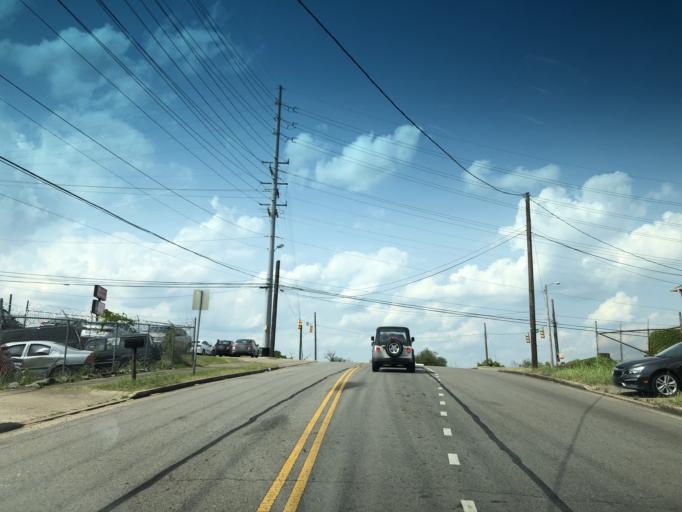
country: US
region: Tennessee
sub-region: Davidson County
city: Goodlettsville
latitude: 36.2627
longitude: -86.7149
